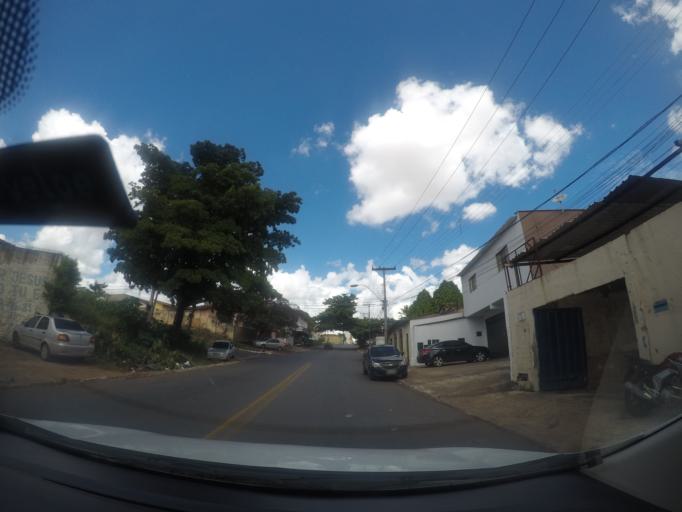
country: BR
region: Goias
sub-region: Goiania
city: Goiania
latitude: -16.6641
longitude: -49.2963
